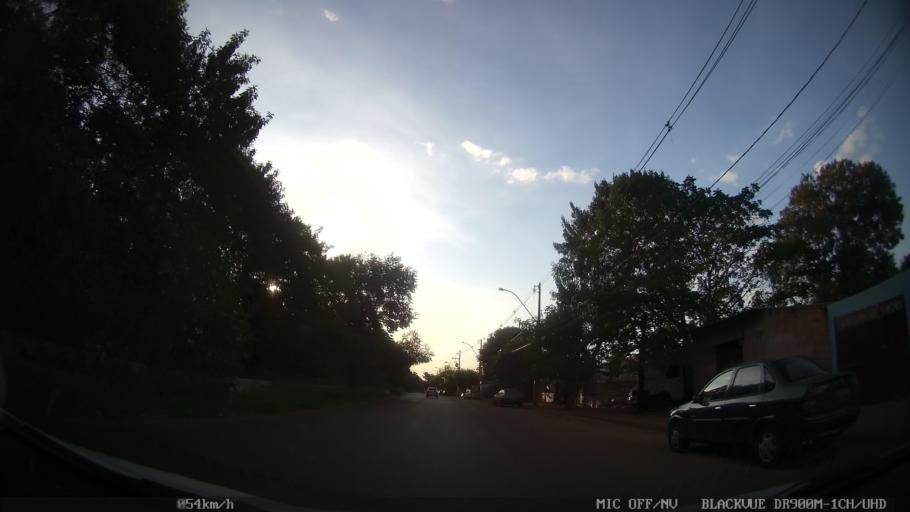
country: BR
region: Sao Paulo
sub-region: Ribeirao Preto
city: Ribeirao Preto
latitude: -21.1147
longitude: -47.8048
